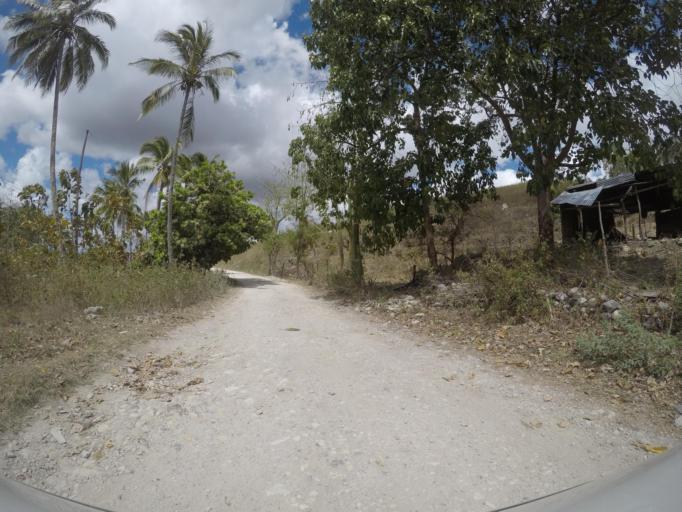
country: TL
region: Baucau
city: Baucau
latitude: -8.5289
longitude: 126.6988
